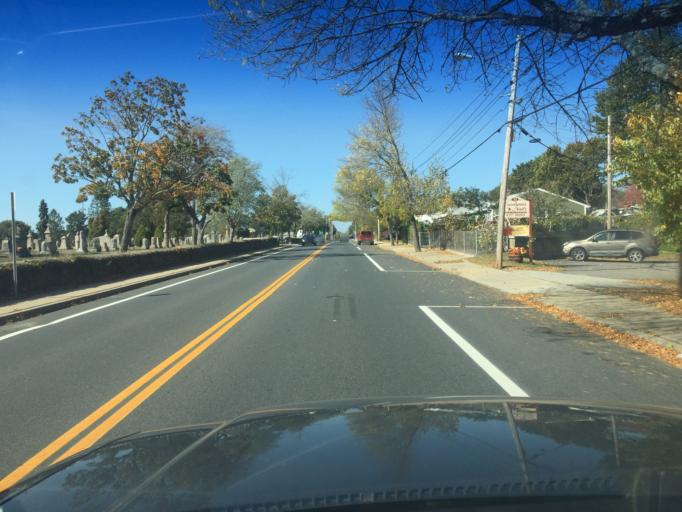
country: US
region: Rhode Island
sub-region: Providence County
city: Pawtucket
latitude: 41.8569
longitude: -71.3642
